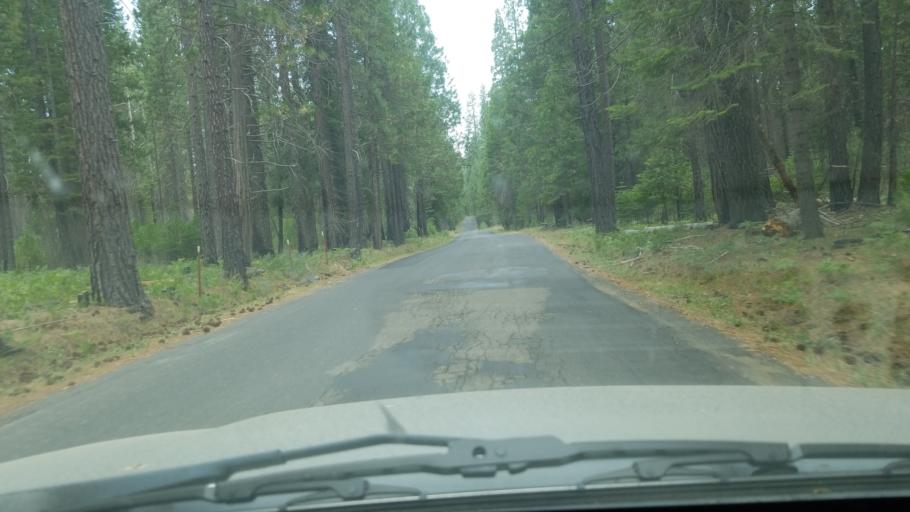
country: US
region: California
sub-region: Mariposa County
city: Yosemite Valley
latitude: 37.8342
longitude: -119.8482
